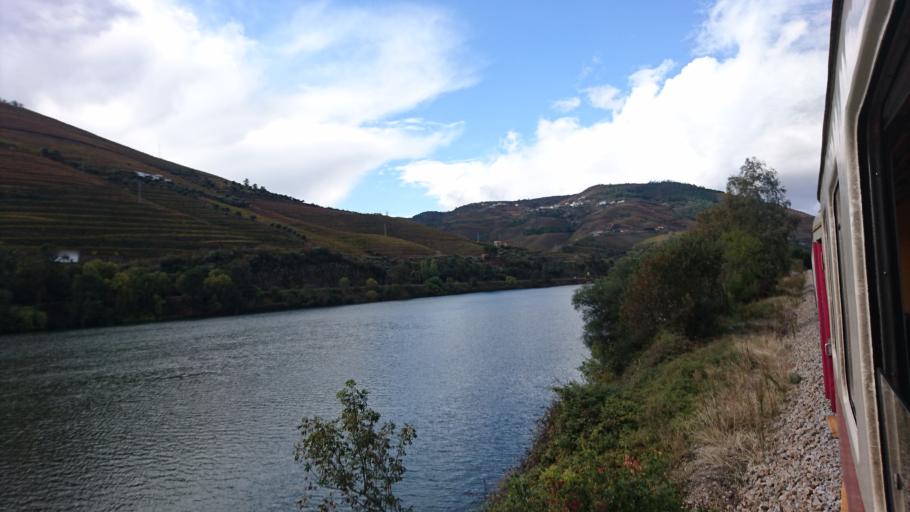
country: PT
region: Vila Real
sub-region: Sabrosa
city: Vilela
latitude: 41.1601
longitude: -7.6294
